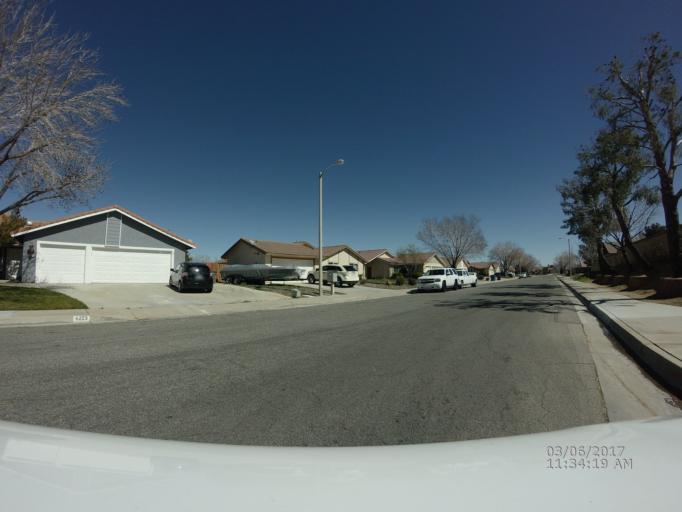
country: US
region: California
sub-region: Los Angeles County
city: Quartz Hill
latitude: 34.6524
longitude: -118.2409
